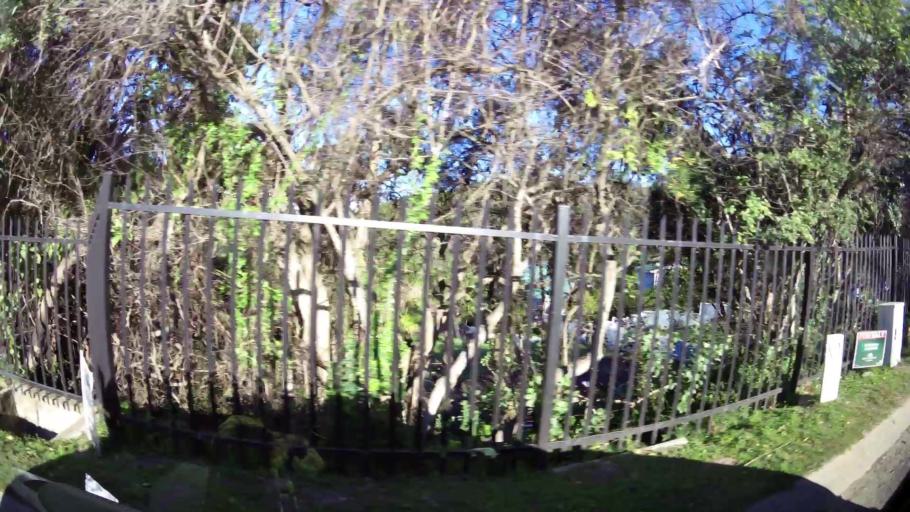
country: ZA
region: Western Cape
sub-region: Eden District Municipality
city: Knysna
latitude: -34.0350
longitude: 23.0158
